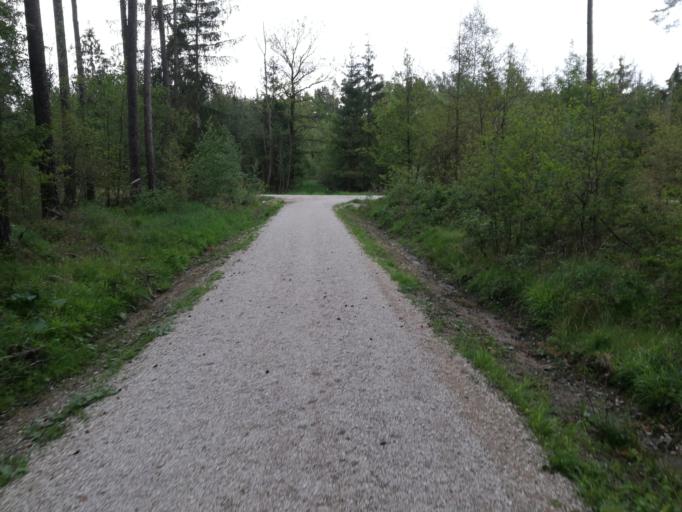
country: DE
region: Bavaria
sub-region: Regierungsbezirk Mittelfranken
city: Seukendorf
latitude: 49.4653
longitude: 10.9039
